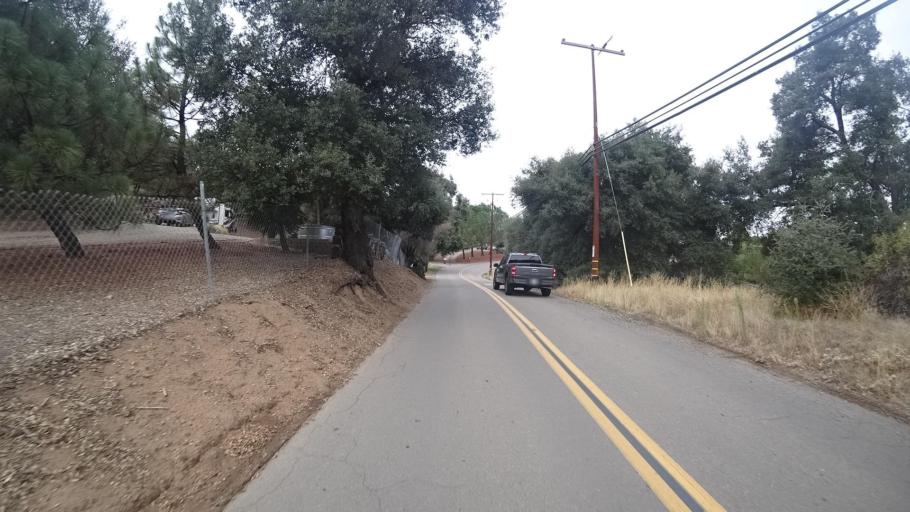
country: US
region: California
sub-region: San Diego County
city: Descanso
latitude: 32.8544
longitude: -116.6160
